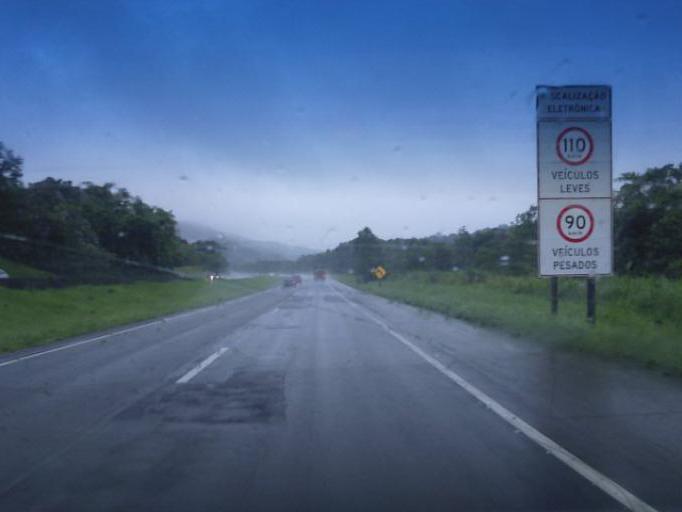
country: BR
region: Sao Paulo
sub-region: Juquia
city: Juquia
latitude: -24.3708
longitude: -47.7021
